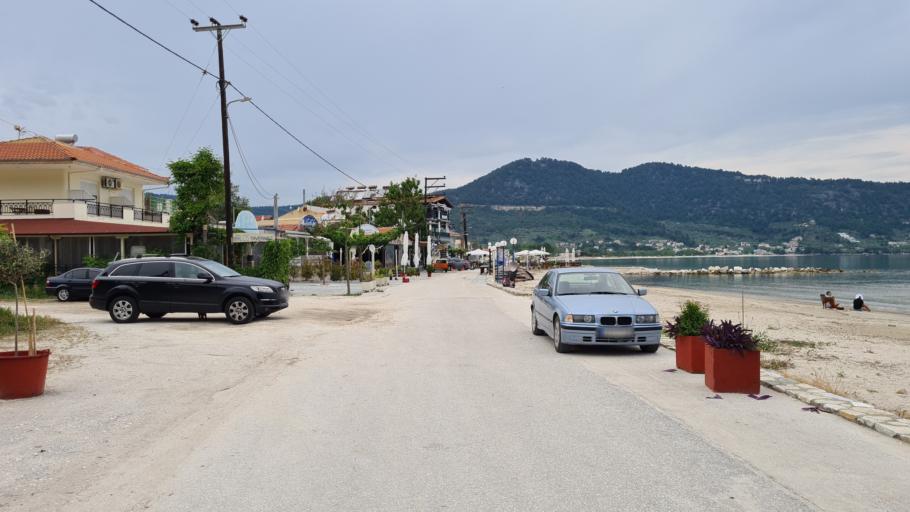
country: GR
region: East Macedonia and Thrace
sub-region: Nomos Kavalas
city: Potamia
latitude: 40.7098
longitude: 24.7594
